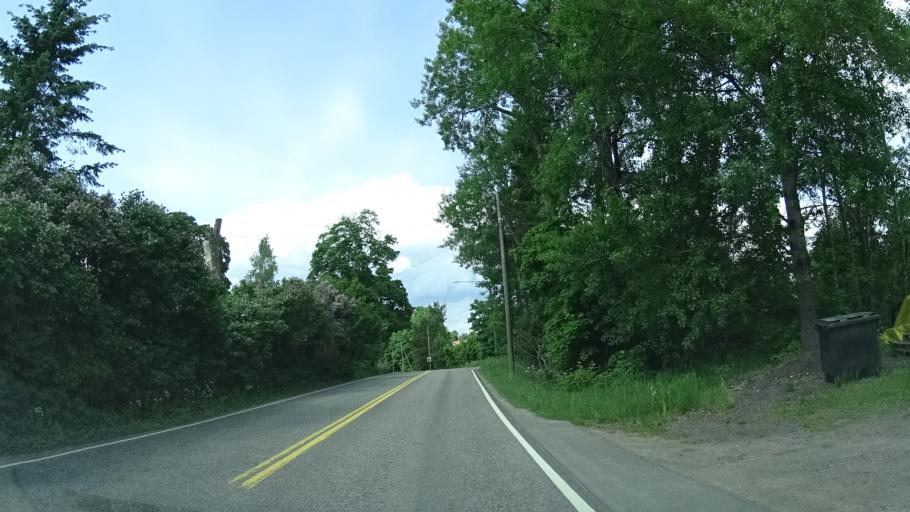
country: FI
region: Uusimaa
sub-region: Helsinki
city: Kirkkonummi
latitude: 60.2203
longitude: 24.4723
